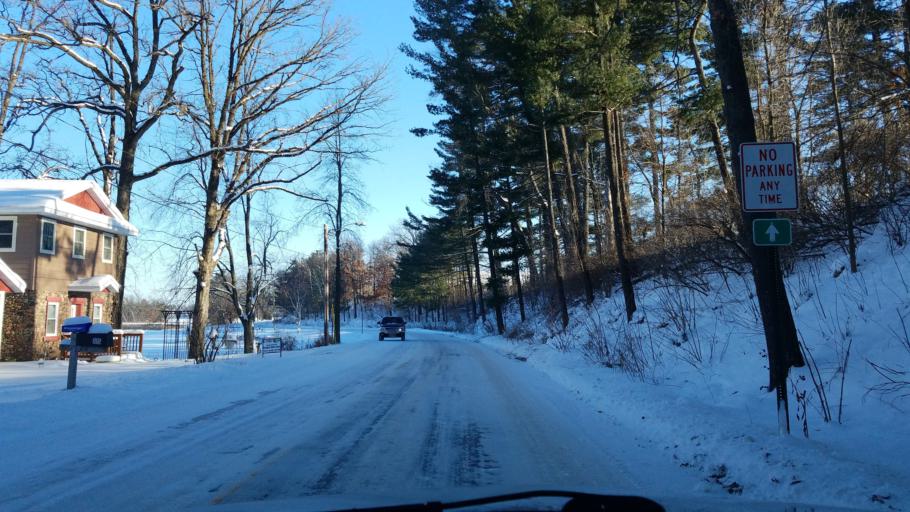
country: US
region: Wisconsin
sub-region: Barron County
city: Rice Lake
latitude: 45.5154
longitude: -91.7378
